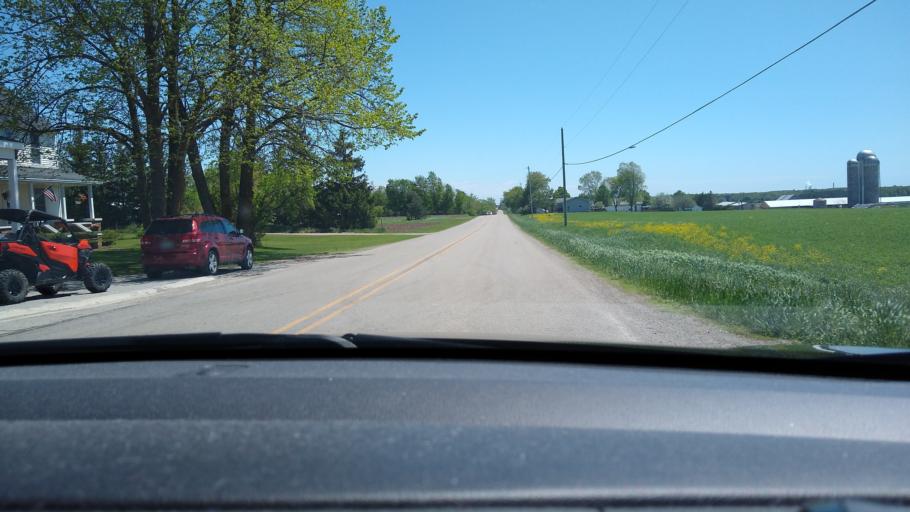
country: US
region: Michigan
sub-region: Delta County
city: Escanaba
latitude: 45.8261
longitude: -87.1627
